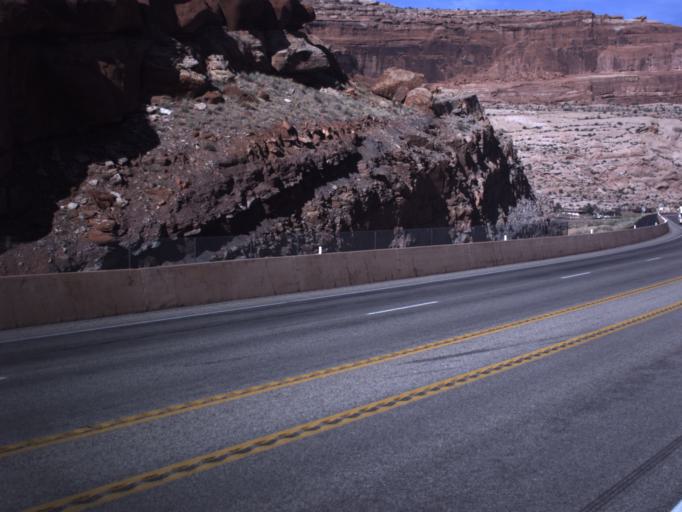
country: US
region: Utah
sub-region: Grand County
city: Moab
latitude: 38.6136
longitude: -109.6234
